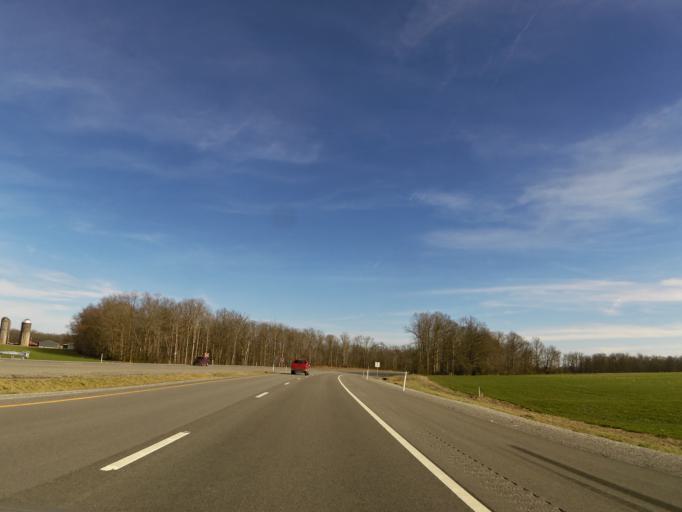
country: US
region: Tennessee
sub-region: Cannon County
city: Woodbury
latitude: 35.7640
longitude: -85.9700
